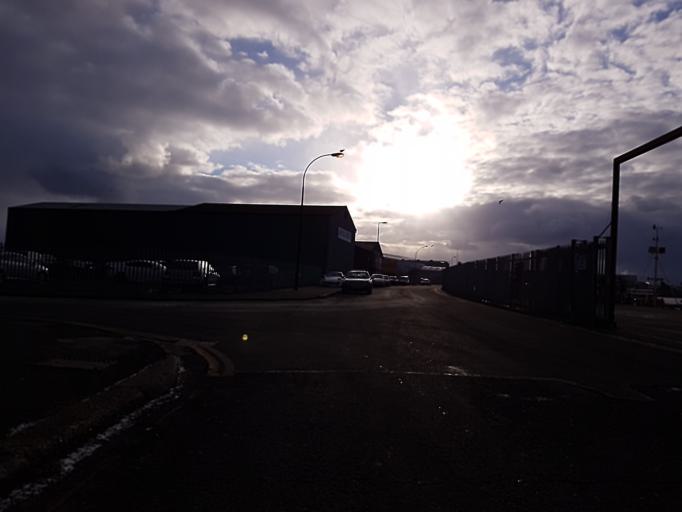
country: GB
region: England
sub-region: North East Lincolnshire
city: Grimsby
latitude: 53.5821
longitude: -0.0638
